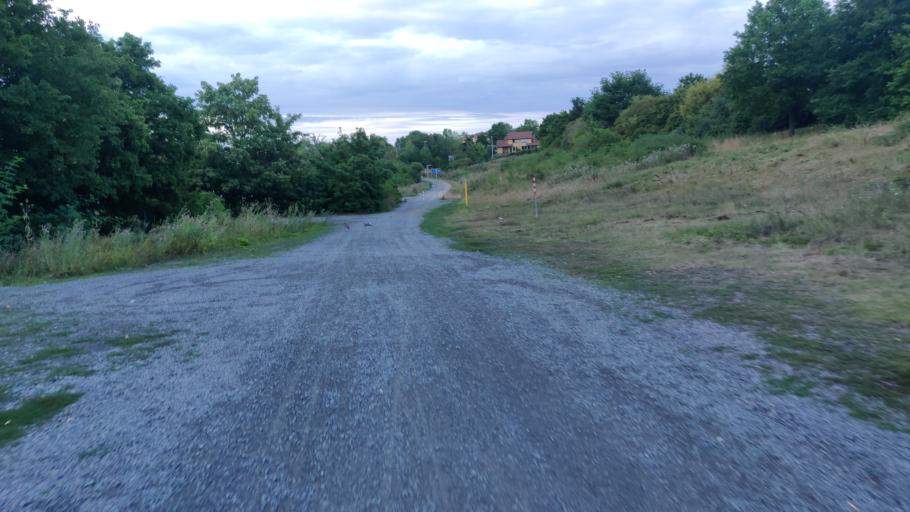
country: DE
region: Bavaria
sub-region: Regierungsbezirk Unterfranken
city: Niederwerrn
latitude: 50.0565
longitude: 10.1984
